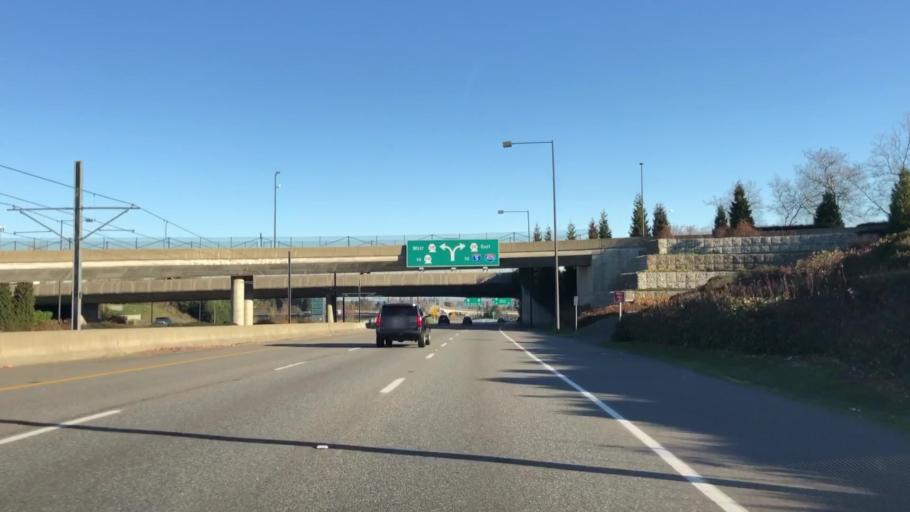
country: US
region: Washington
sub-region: King County
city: SeaTac
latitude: 47.4588
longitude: -122.2987
